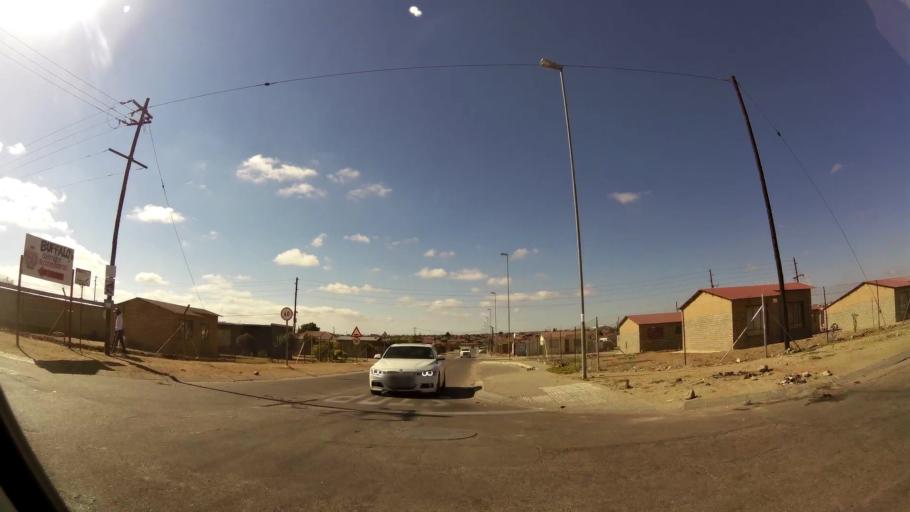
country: ZA
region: Limpopo
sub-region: Capricorn District Municipality
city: Polokwane
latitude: -23.8598
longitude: 29.3960
